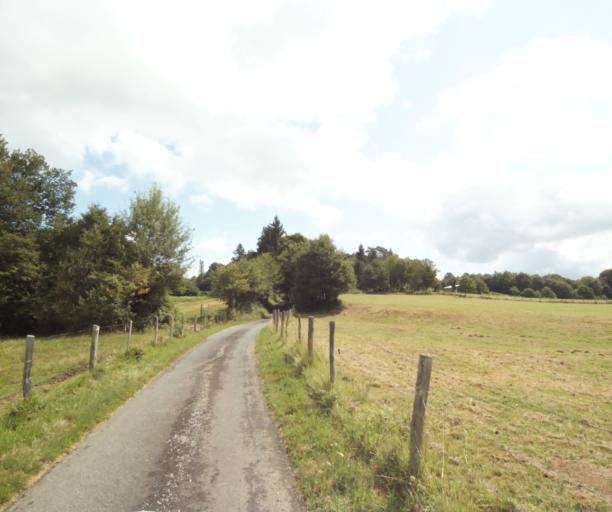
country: FR
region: Limousin
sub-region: Departement de la Correze
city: Sainte-Fortunade
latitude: 45.1722
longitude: 1.7842
